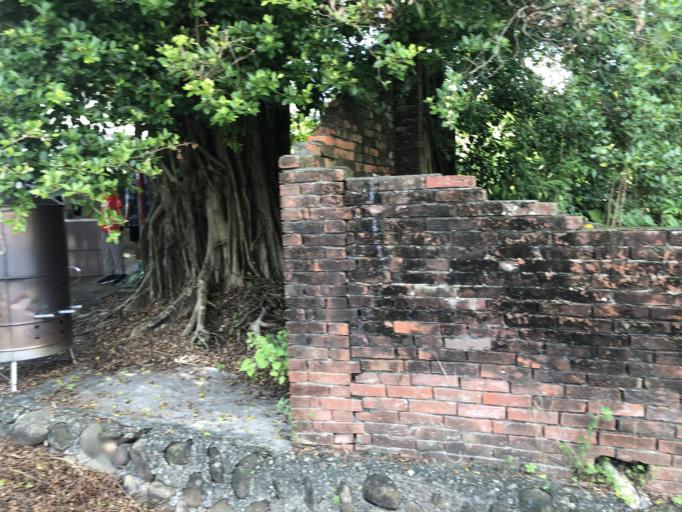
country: TW
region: Taiwan
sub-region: Pingtung
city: Pingtung
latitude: 22.8983
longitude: 120.5497
